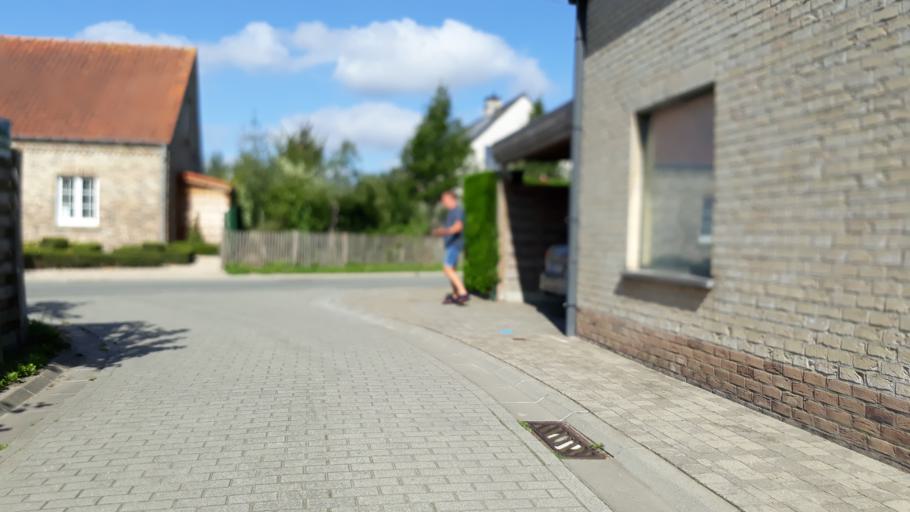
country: BE
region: Flanders
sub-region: Provincie West-Vlaanderen
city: Torhout
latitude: 51.0579
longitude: 3.1218
